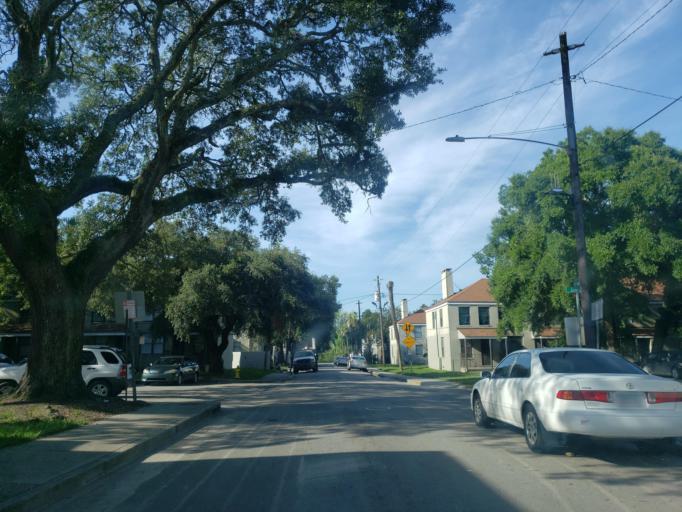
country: US
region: Georgia
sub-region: Chatham County
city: Savannah
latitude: 32.0815
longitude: -81.1018
